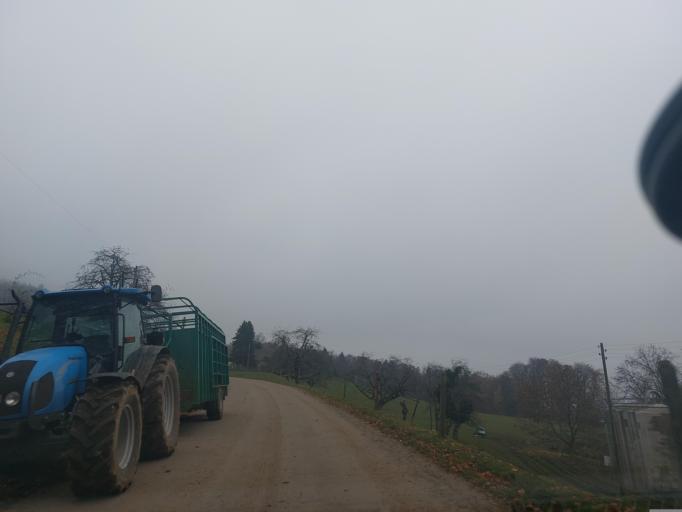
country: CH
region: Vaud
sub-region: Riviera-Pays-d'Enhaut District
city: Blonay
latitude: 46.4953
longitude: 6.8932
